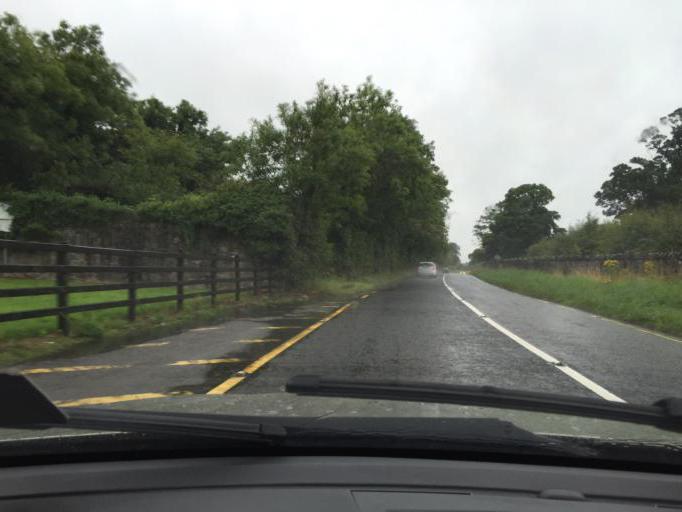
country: IE
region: Leinster
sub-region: Kildare
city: Maynooth
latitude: 53.3783
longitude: -6.5574
